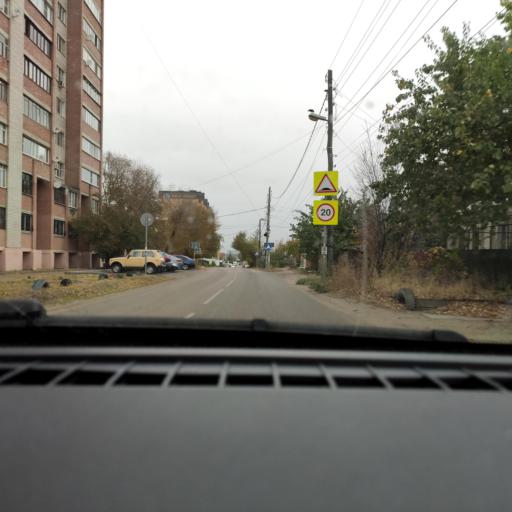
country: RU
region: Voronezj
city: Voronezh
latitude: 51.6631
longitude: 39.2801
